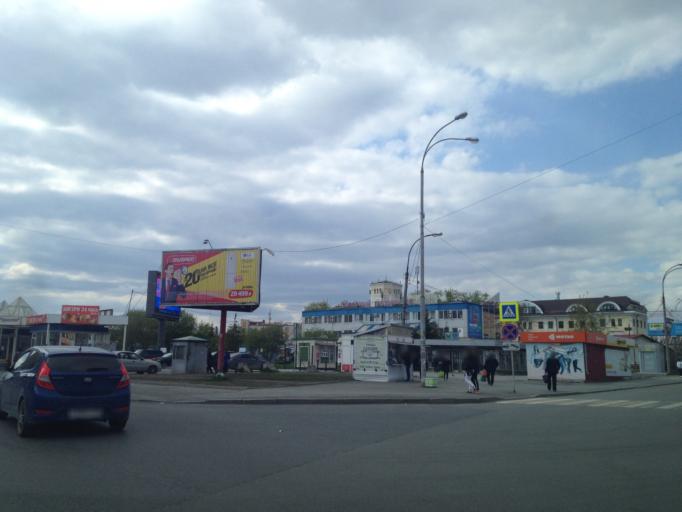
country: RU
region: Sverdlovsk
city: Yekaterinburg
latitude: 56.8571
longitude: 60.6007
